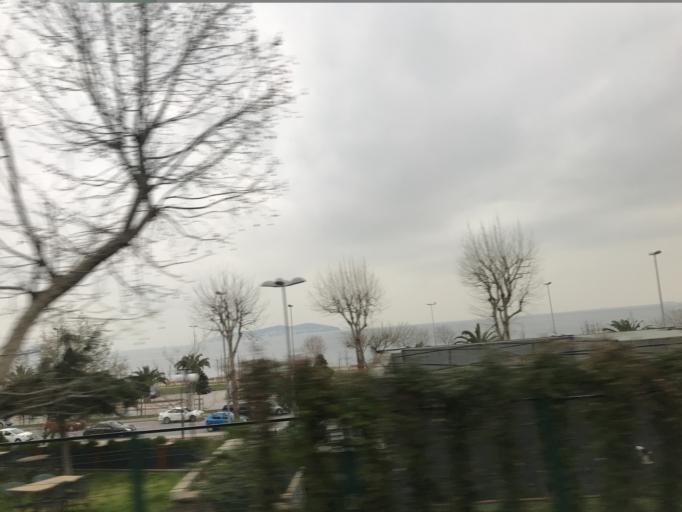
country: TR
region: Istanbul
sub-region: Atasehir
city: Atasehir
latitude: 40.9479
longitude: 29.1023
